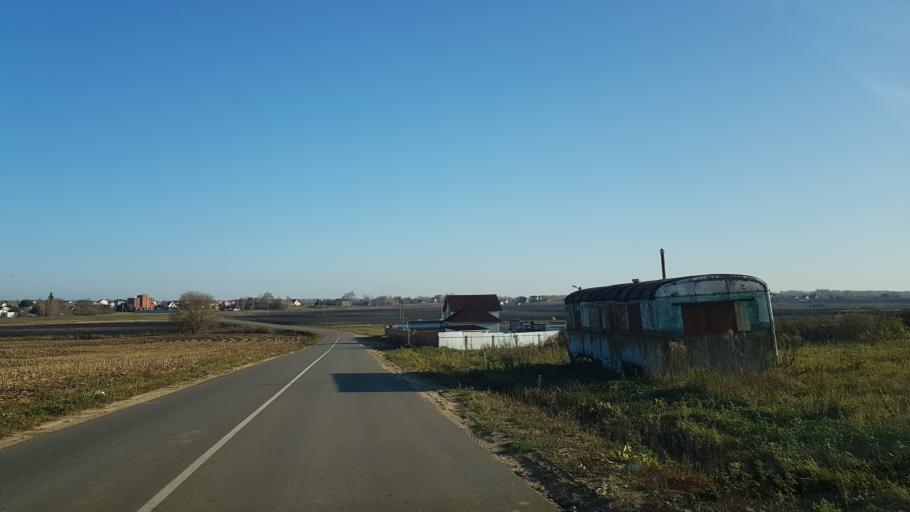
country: BY
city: Fanipol
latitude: 53.7213
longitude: 27.3034
